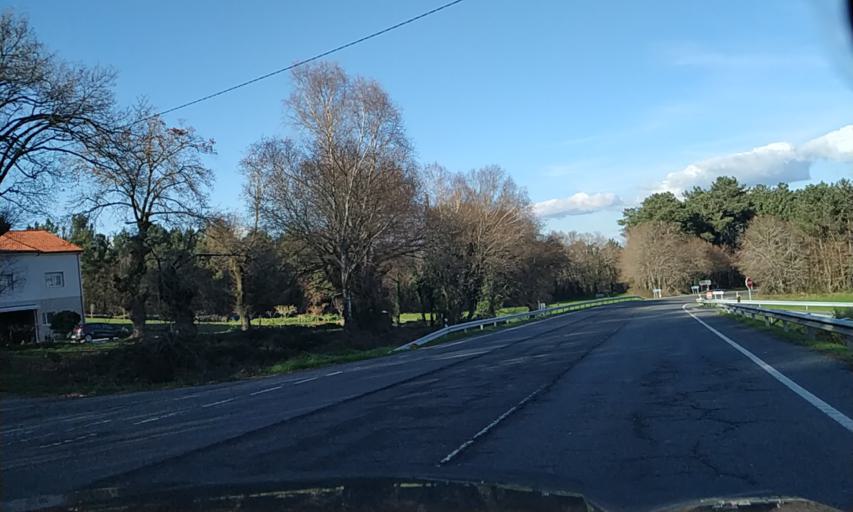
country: ES
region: Galicia
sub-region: Provincia de Pontevedra
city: Silleda
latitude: 42.7031
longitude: -8.3108
